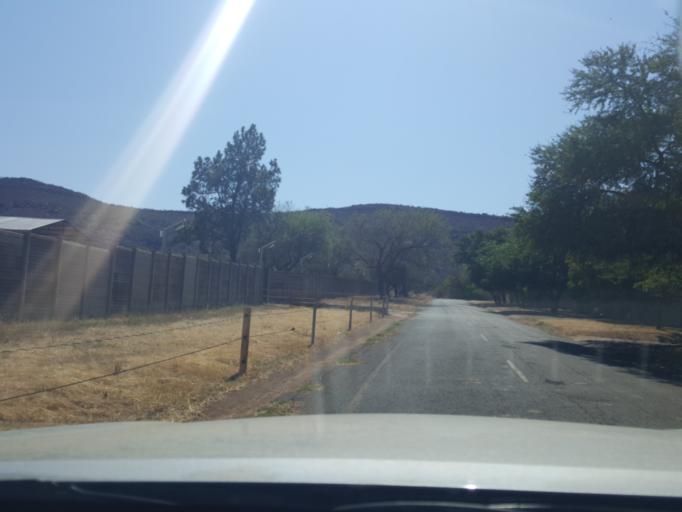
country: ZA
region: North-West
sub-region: Ngaka Modiri Molema District Municipality
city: Zeerust
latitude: -25.5248
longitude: 26.0783
